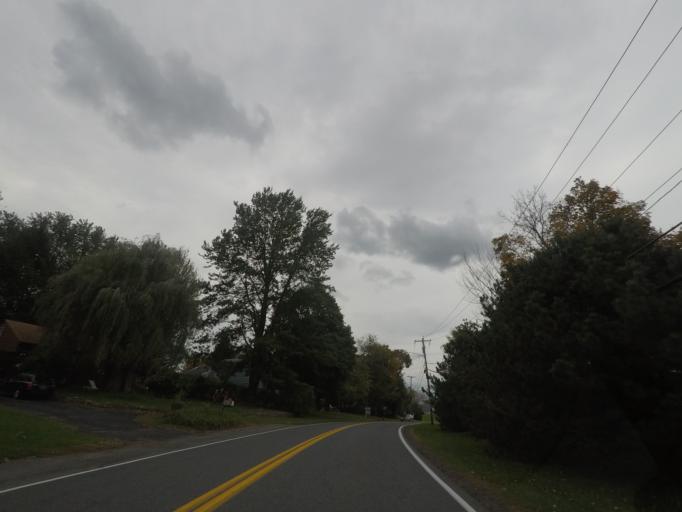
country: US
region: New York
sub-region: Albany County
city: McKownville
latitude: 42.6602
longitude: -73.8376
